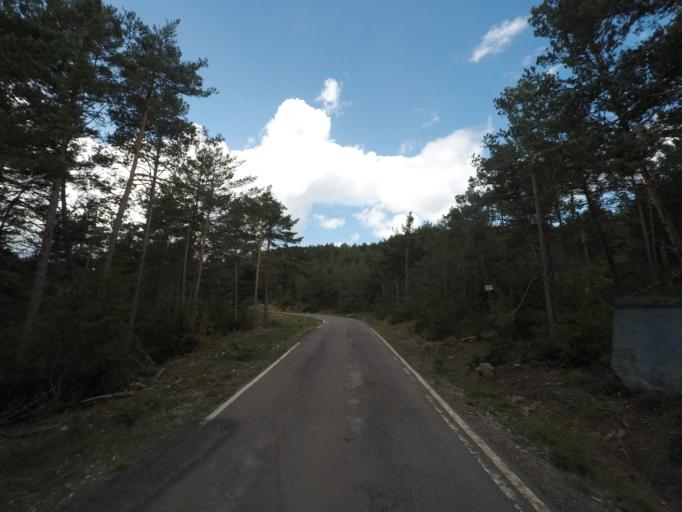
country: ES
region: Aragon
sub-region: Provincia de Huesca
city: Fiscal
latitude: 42.4057
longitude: -0.0834
